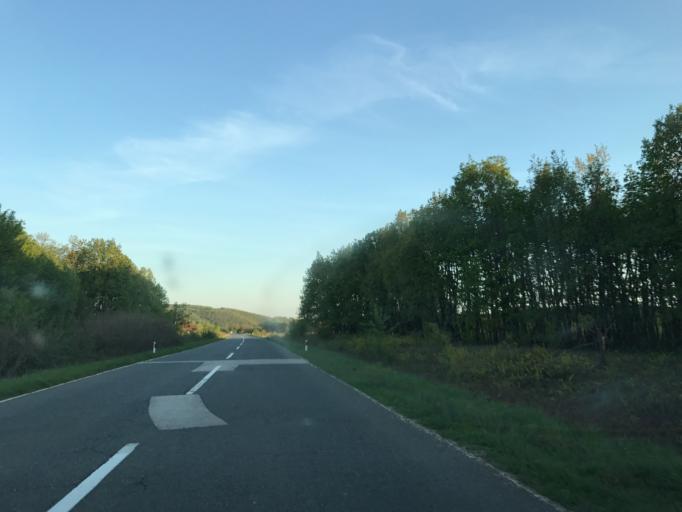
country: RO
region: Mehedinti
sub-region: Comuna Gogosu
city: Ostrovu Mare
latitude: 44.4433
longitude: 22.4556
